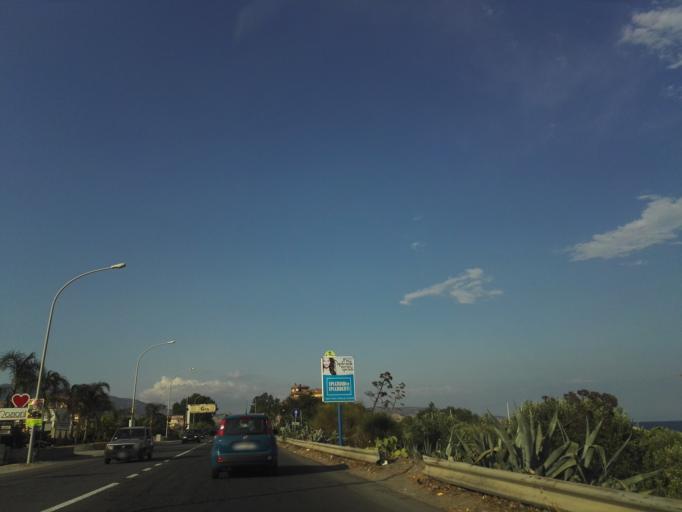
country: IT
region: Calabria
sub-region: Provincia di Reggio Calabria
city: Marina di Gioiosa Ionica
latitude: 38.2900
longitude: 16.3177
